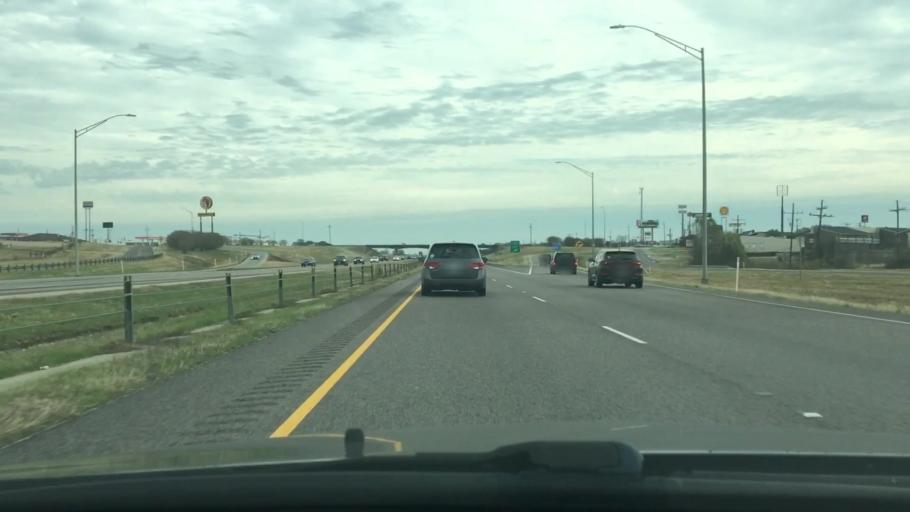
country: US
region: Texas
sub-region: Madison County
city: Madisonville
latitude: 30.9688
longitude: -95.8861
